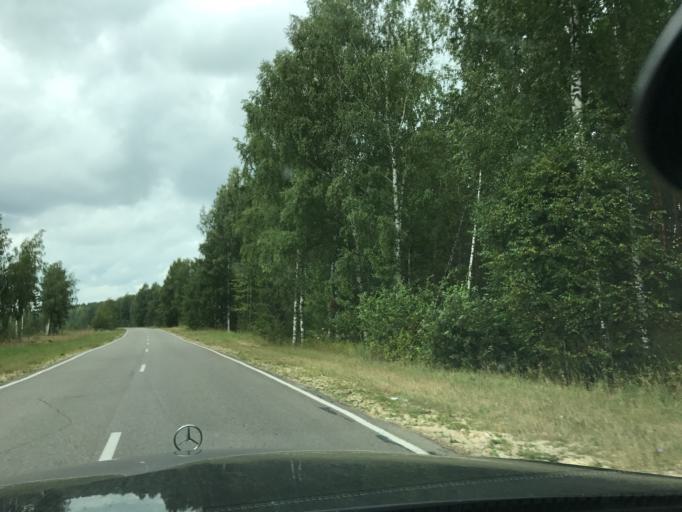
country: RU
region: Nizjnij Novgorod
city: Taremskoye
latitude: 56.0145
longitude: 42.9552
